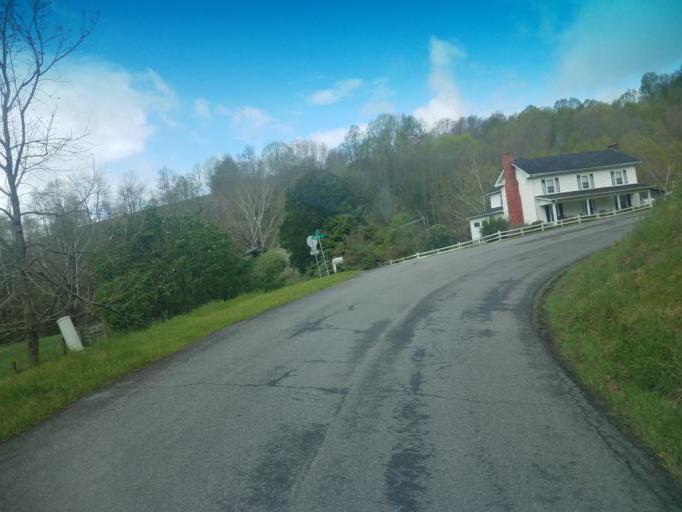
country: US
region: Virginia
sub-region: Smyth County
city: Atkins
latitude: 36.9744
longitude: -81.3965
